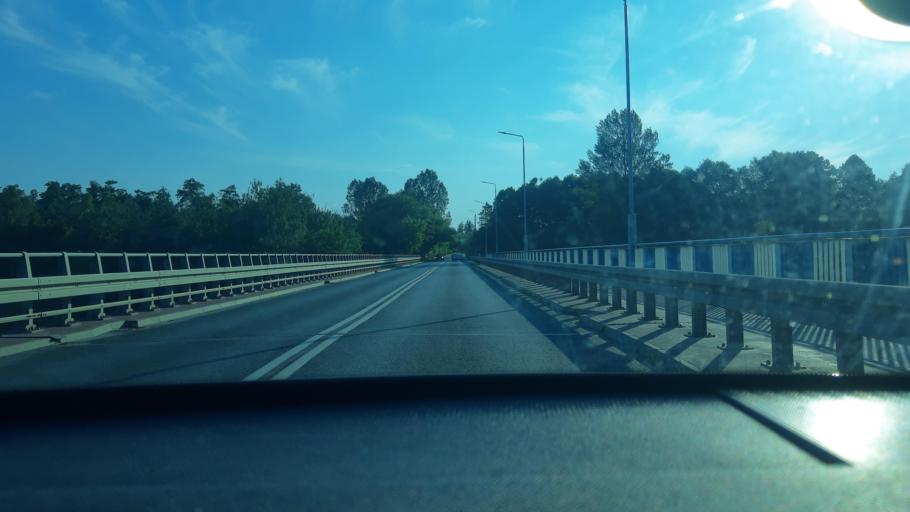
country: PL
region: Lodz Voivodeship
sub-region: Powiat sieradzki
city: Burzenin
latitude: 51.4588
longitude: 18.8381
